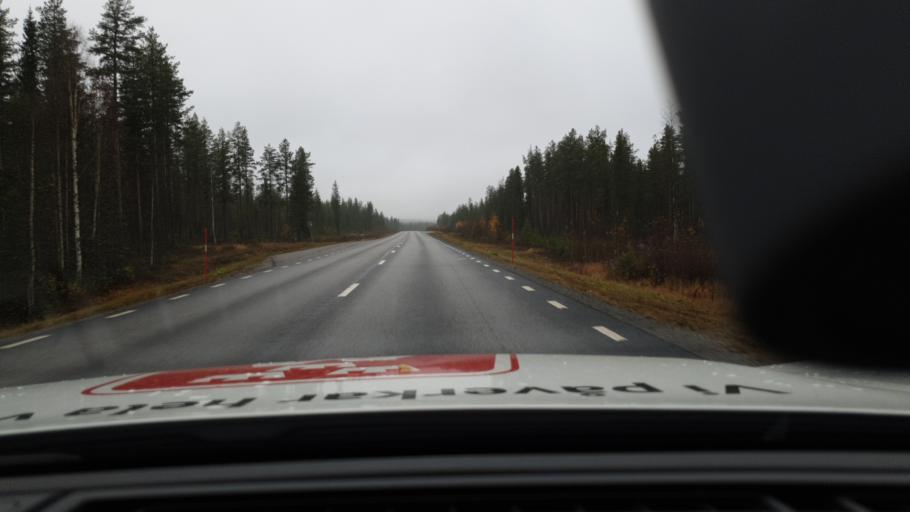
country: SE
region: Norrbotten
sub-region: Overkalix Kommun
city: OEverkalix
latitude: 66.6266
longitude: 22.2191
